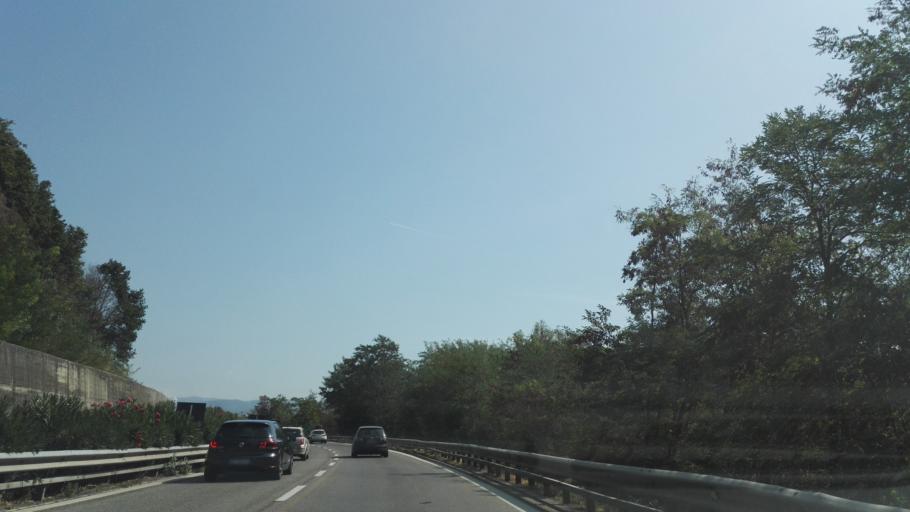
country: IT
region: Calabria
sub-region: Provincia di Cosenza
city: Altilia
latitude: 39.1307
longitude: 16.2679
